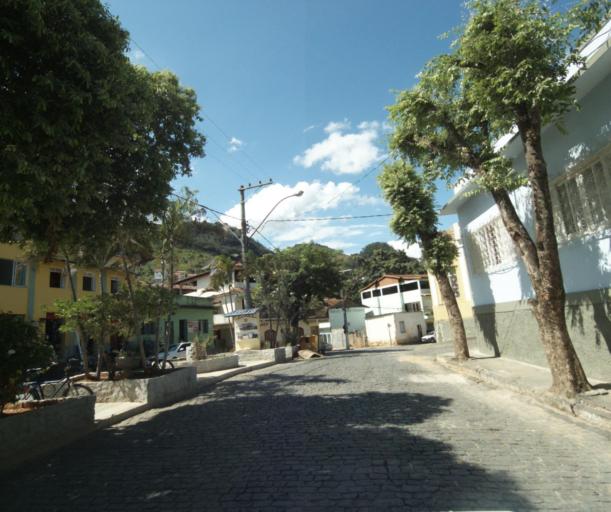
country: BR
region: Espirito Santo
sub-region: Mimoso Do Sul
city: Mimoso do Sul
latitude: -21.0594
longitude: -41.3619
